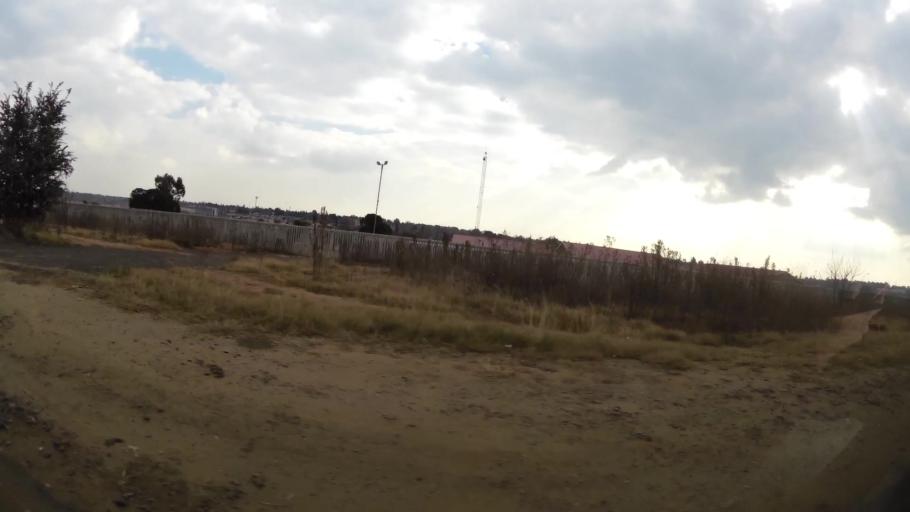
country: ZA
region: Gauteng
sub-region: Ekurhuleni Metropolitan Municipality
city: Benoni
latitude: -26.1401
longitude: 28.3569
